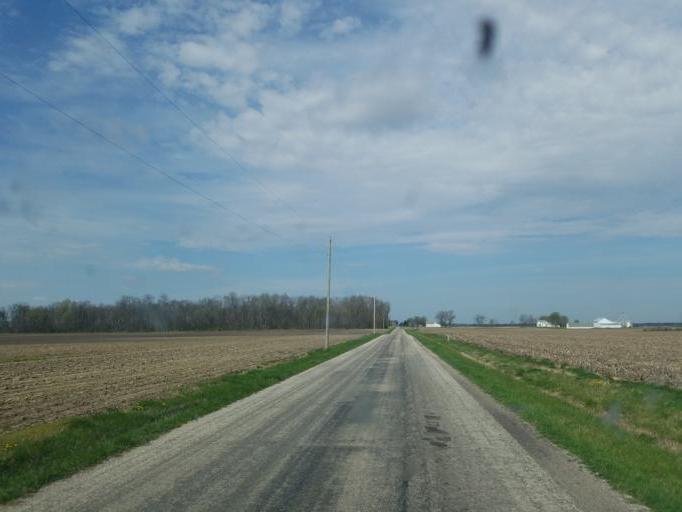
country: US
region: Ohio
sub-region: Crawford County
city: Bucyrus
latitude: 40.7467
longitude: -82.9940
